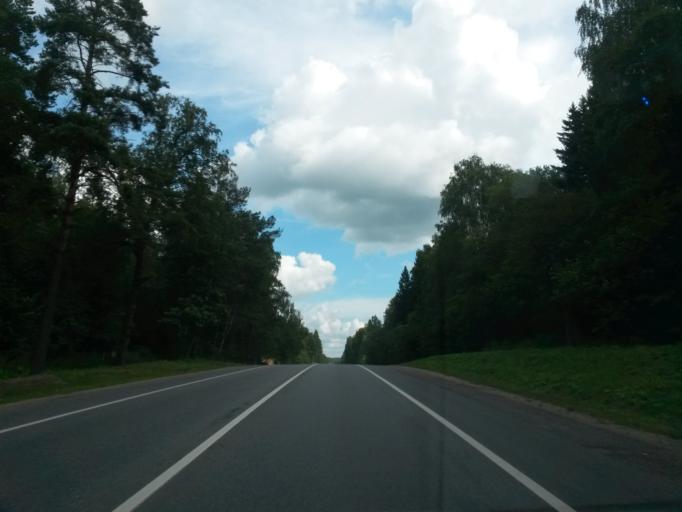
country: RU
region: Jaroslavl
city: Pereslavl'-Zalesskiy
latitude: 56.6749
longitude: 38.7284
